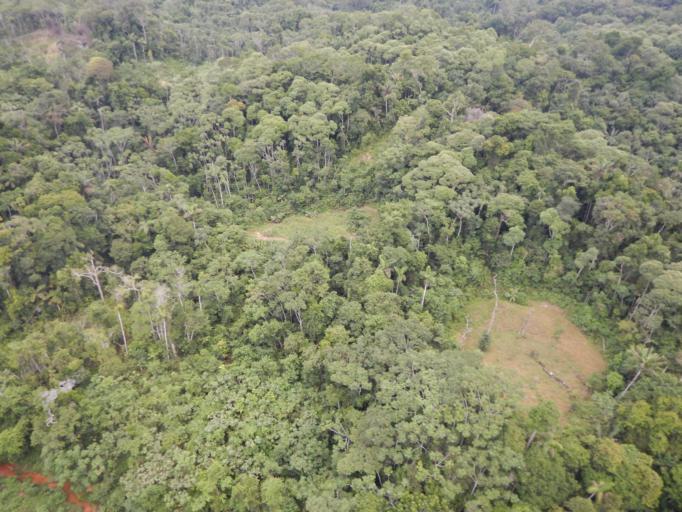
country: BO
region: Cochabamba
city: Chimore
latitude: -17.0292
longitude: -64.9509
